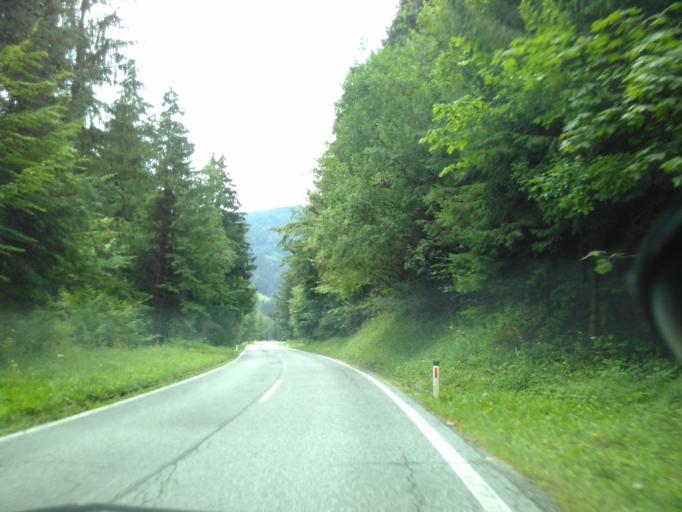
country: AT
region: Styria
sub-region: Politischer Bezirk Graz-Umgebung
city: Rothelstein
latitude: 47.2807
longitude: 15.3915
